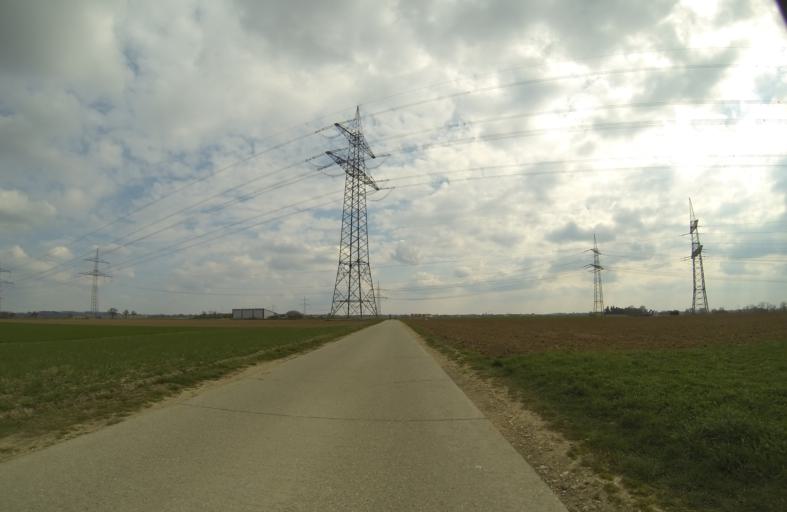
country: DE
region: Baden-Wuerttemberg
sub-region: Tuebingen Region
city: Erbach
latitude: 48.2960
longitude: 9.9012
